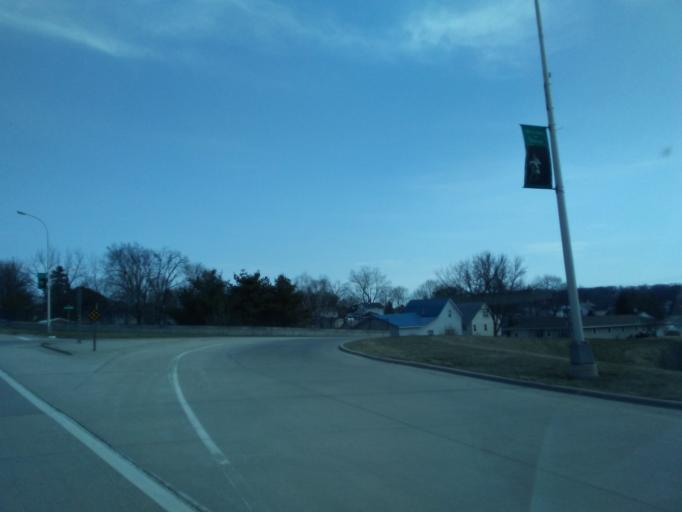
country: US
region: Minnesota
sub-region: Fillmore County
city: Preston
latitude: 43.6755
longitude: -92.0838
